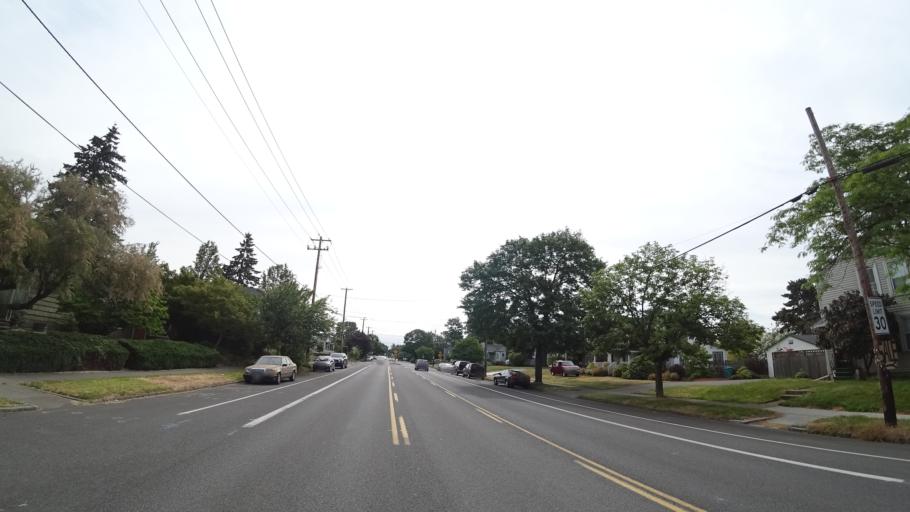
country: US
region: Oregon
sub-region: Multnomah County
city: Portland
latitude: 45.5699
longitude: -122.6863
